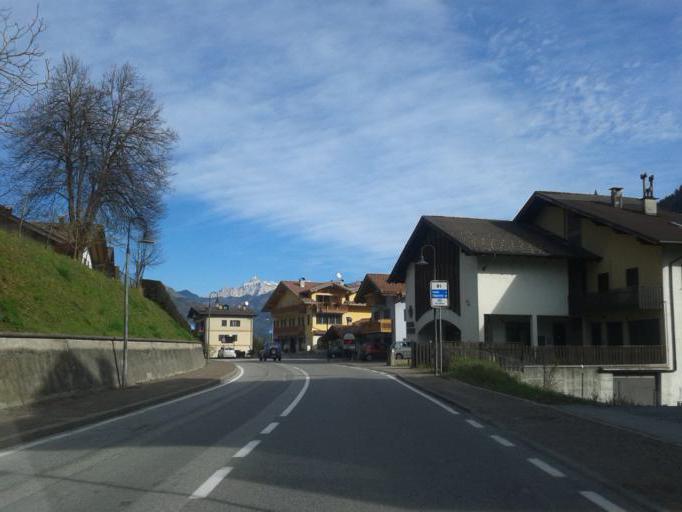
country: IT
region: Trentino-Alto Adige
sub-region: Provincia di Trento
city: Bondo
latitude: 46.0031
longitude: 10.6946
